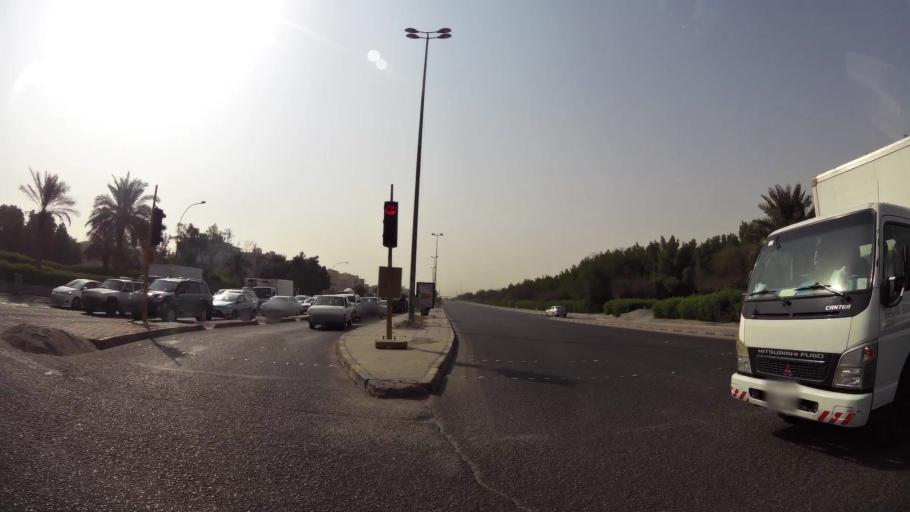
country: KW
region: Al Asimah
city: Ar Rabiyah
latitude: 29.2746
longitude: 47.8644
